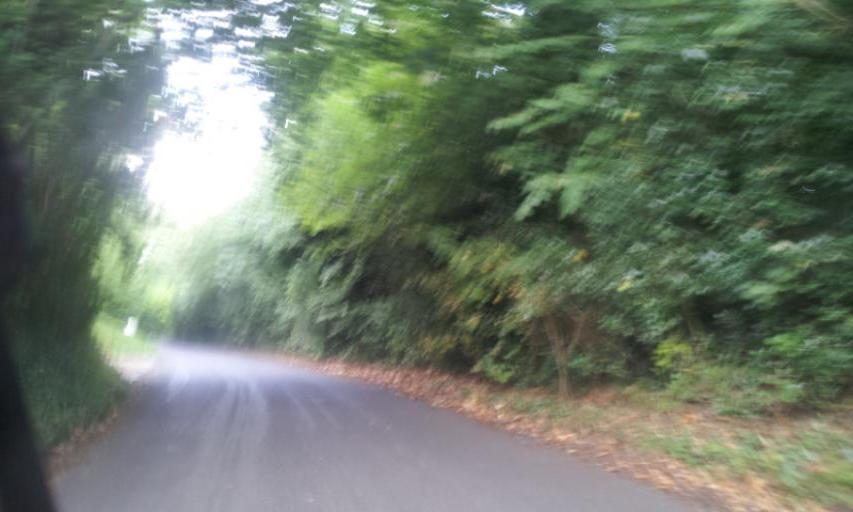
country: GB
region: England
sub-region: Kent
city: Paddock Wood
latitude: 51.1524
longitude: 0.3609
